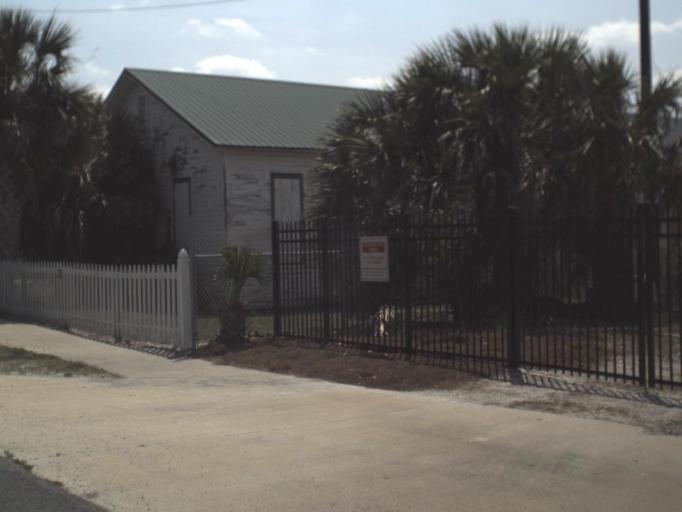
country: US
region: Florida
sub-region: Duval County
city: Atlantic Beach
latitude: 30.3934
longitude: -81.4307
